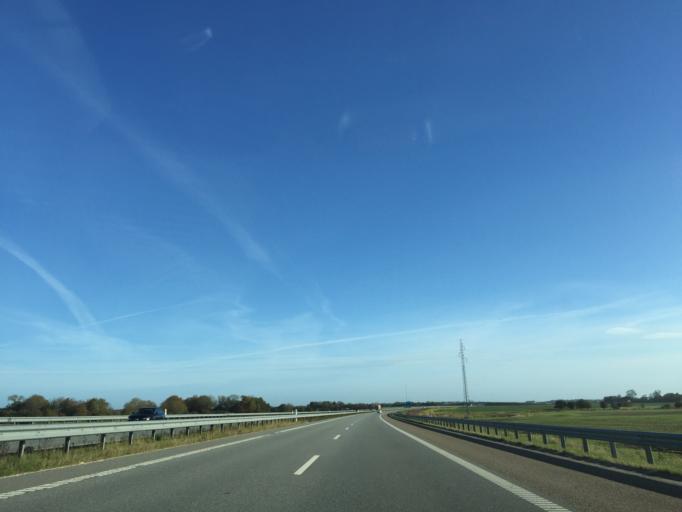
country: DK
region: South Denmark
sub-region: Aabenraa Kommune
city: Aabenraa
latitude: 54.9487
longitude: 9.4814
